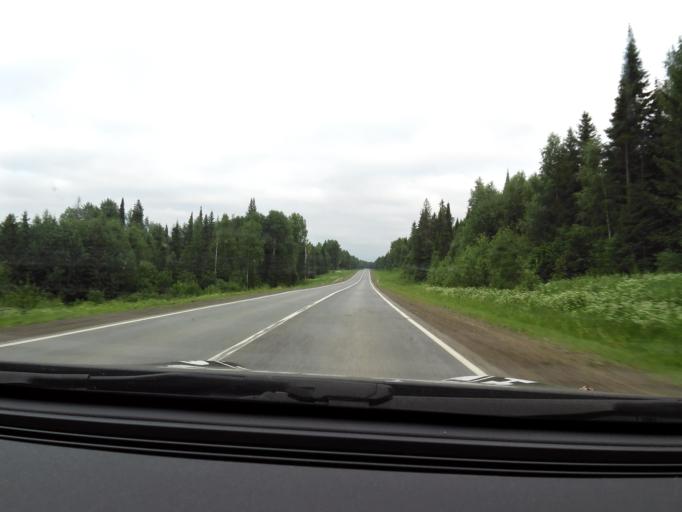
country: RU
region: Perm
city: Zyukayka
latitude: 58.3628
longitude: 54.6871
